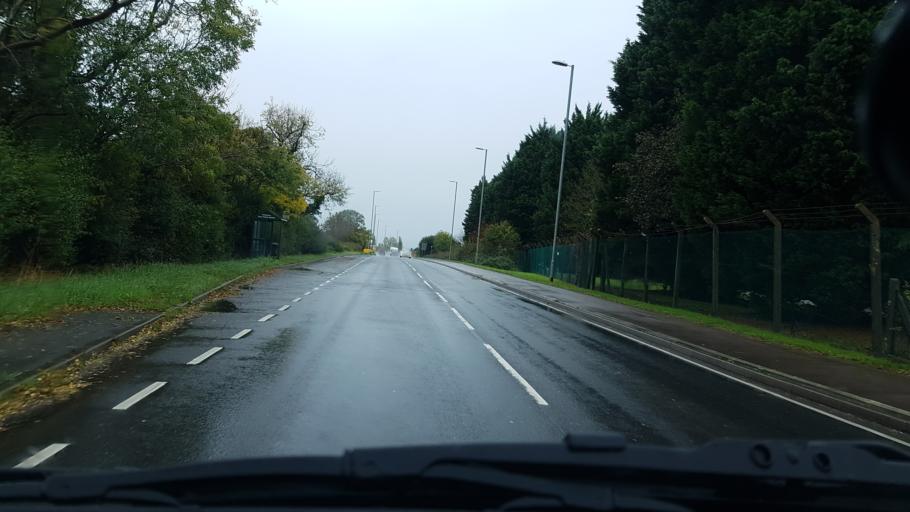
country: GB
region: England
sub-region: Worcestershire
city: Bredon
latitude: 52.0012
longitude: -2.0889
